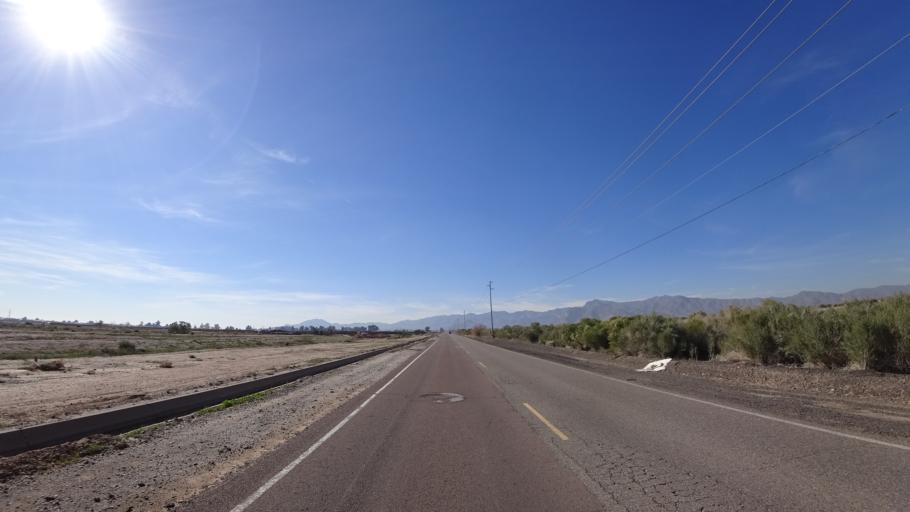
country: US
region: Arizona
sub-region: Maricopa County
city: Citrus Park
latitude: 33.5082
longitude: -112.4507
